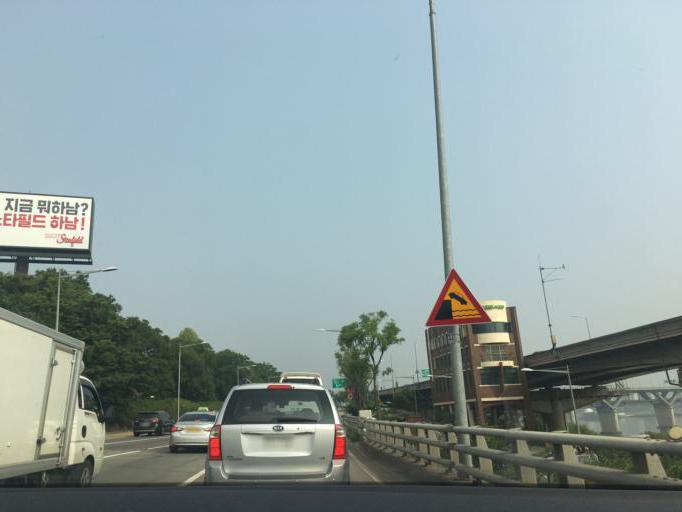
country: KR
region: Seoul
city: Seoul
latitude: 37.5194
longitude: 127.0649
